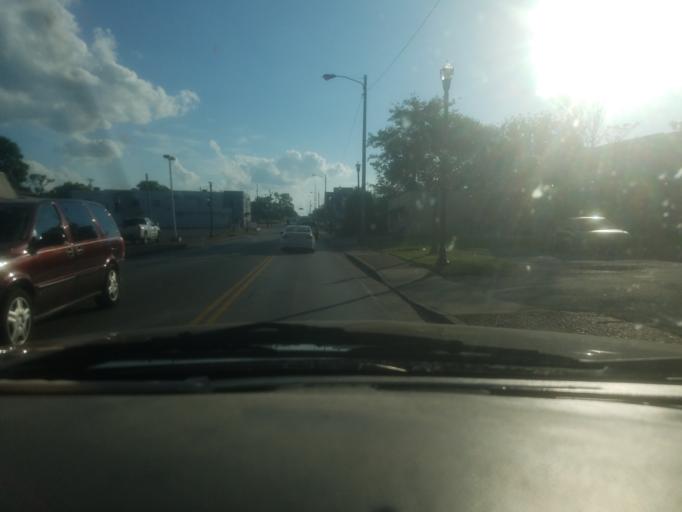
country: US
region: Tennessee
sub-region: Davidson County
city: Nashville
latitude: 36.1724
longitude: -86.7952
